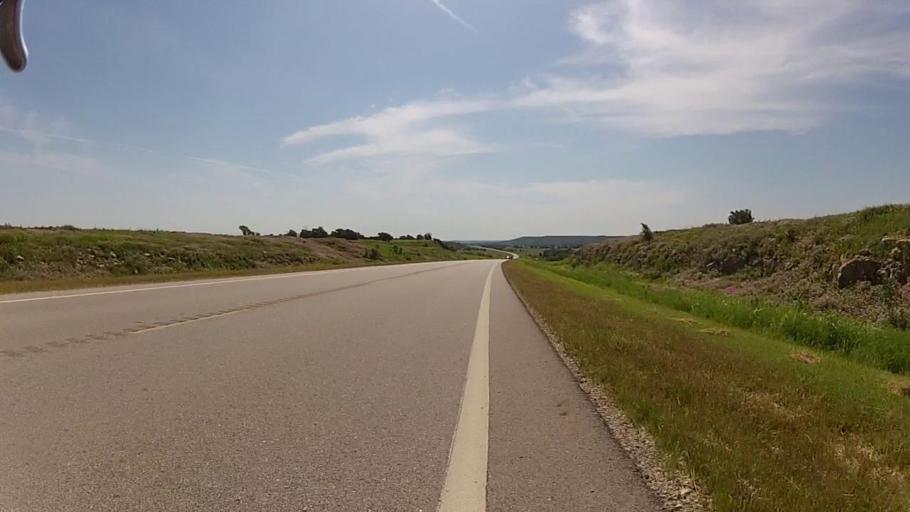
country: US
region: Kansas
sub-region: Chautauqua County
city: Sedan
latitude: 37.1102
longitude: -96.5977
